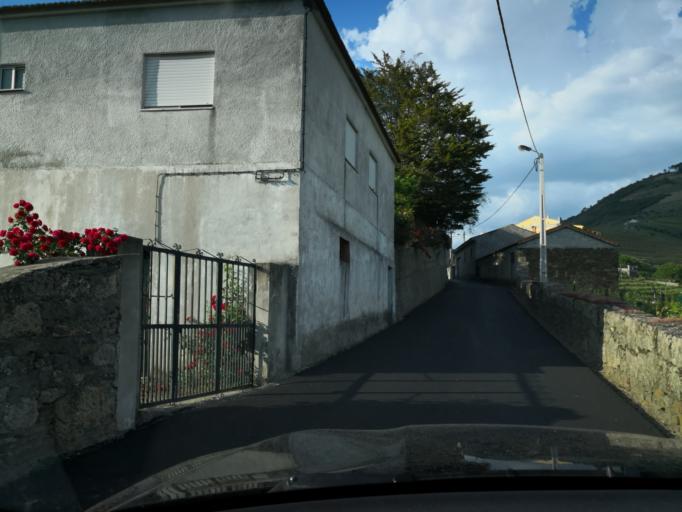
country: PT
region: Vila Real
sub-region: Santa Marta de Penaguiao
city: Santa Marta de Penaguiao
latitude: 41.2178
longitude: -7.7179
